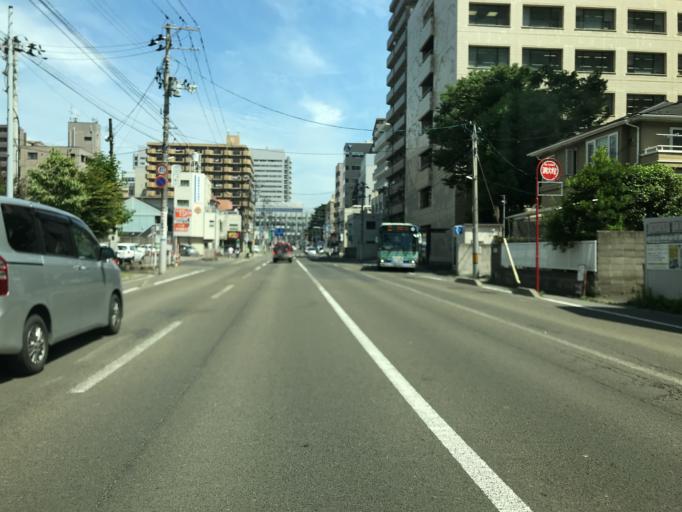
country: JP
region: Miyagi
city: Sendai-shi
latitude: 38.2686
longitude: 140.8624
